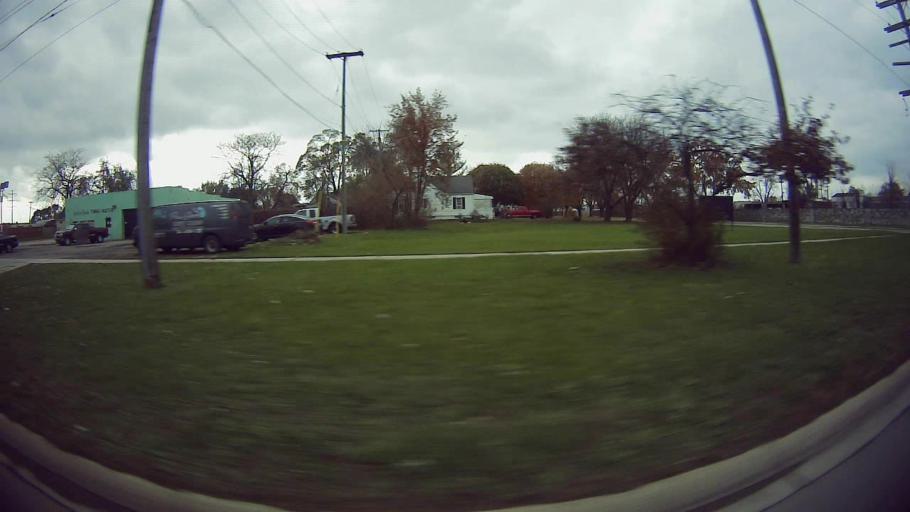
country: US
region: Michigan
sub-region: Macomb County
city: Warren
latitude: 42.4517
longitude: -83.0054
